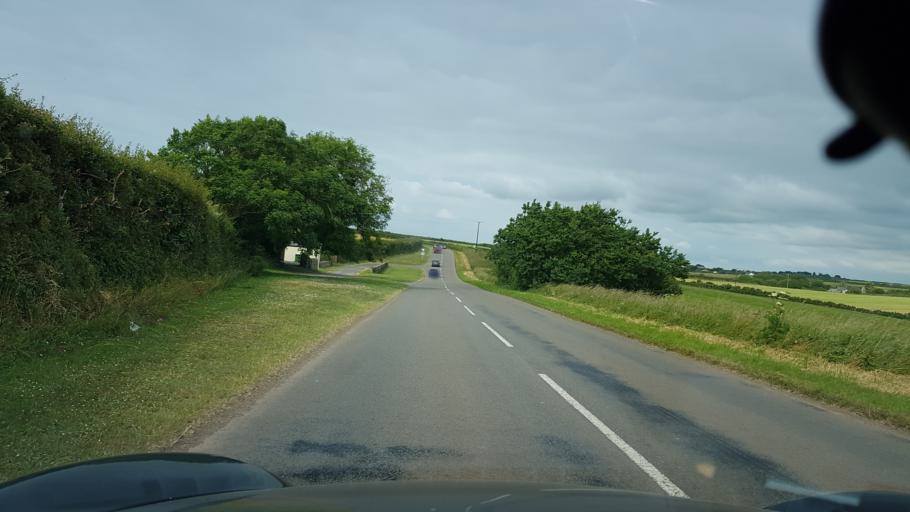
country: GB
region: Wales
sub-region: Pembrokeshire
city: Dale
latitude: 51.7478
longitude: -5.1431
